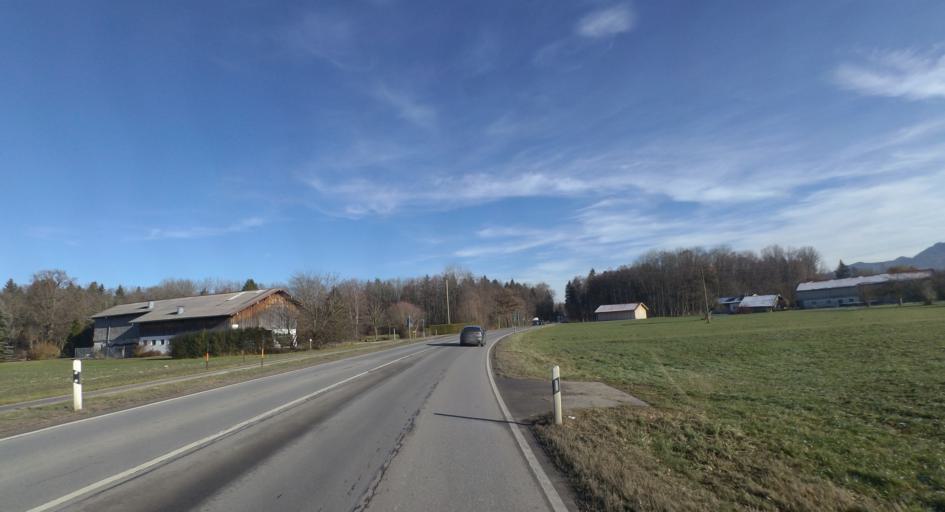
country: DE
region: Bavaria
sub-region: Upper Bavaria
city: Ubersee
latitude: 47.8190
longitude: 12.4968
